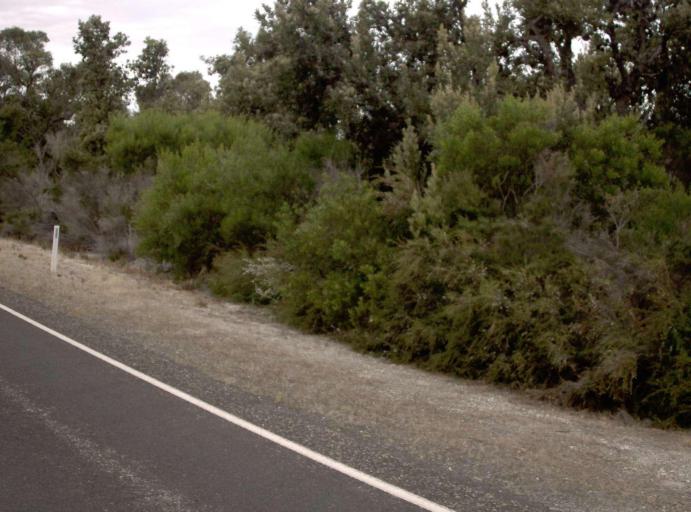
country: AU
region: Victoria
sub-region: Wellington
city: Sale
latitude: -38.1864
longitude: 147.3710
